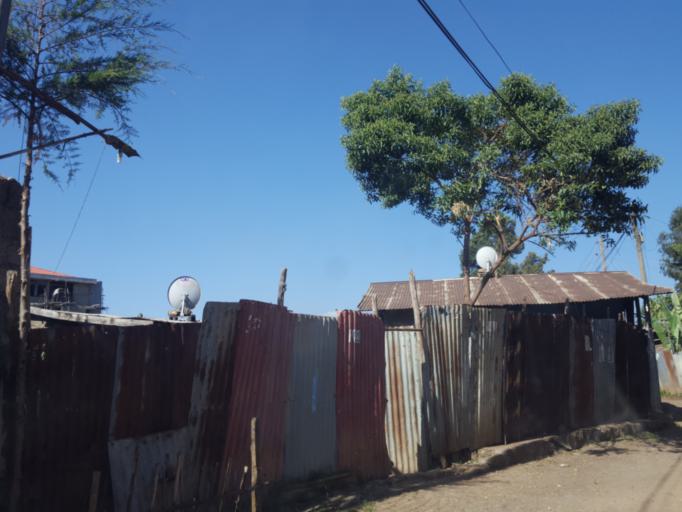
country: ET
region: Adis Abeba
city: Addis Ababa
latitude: 9.0590
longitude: 38.7309
